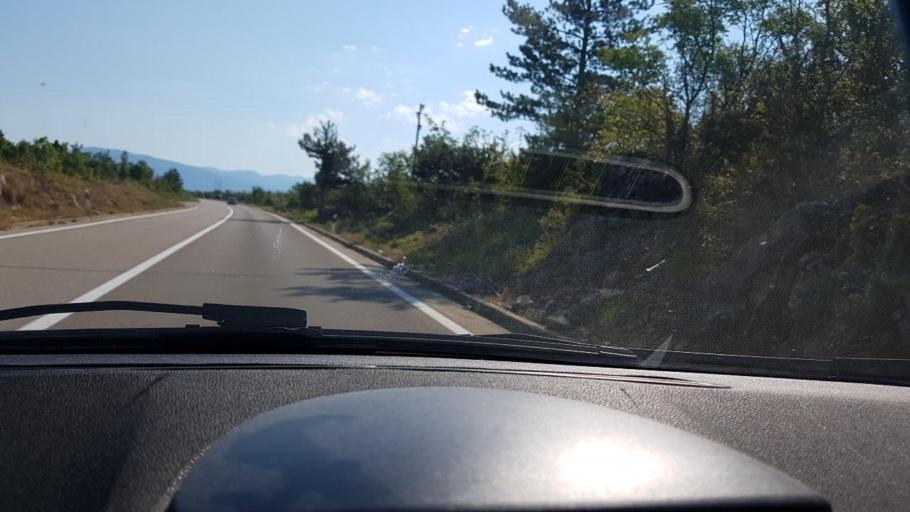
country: HR
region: Sibensko-Kniniska
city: Knin
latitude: 44.0403
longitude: 16.1255
